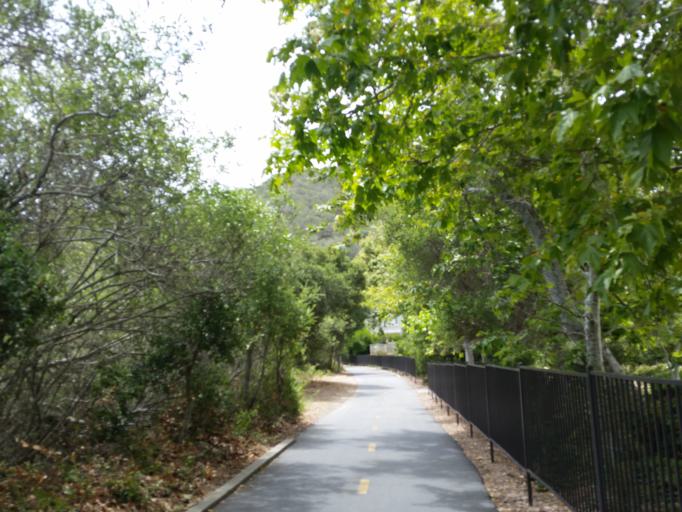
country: US
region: California
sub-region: San Luis Obispo County
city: Avila Beach
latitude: 35.1890
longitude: -120.7246
